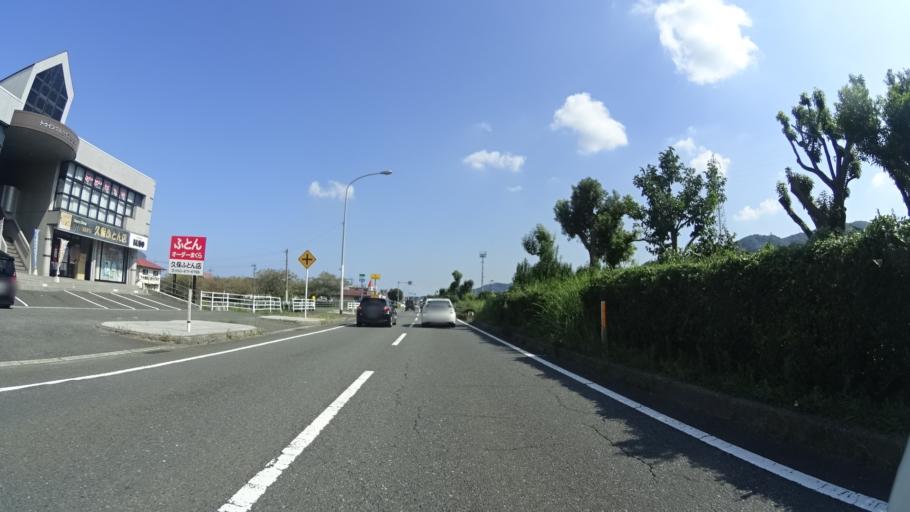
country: JP
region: Fukuoka
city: Kanda
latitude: 33.8151
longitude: 130.9386
